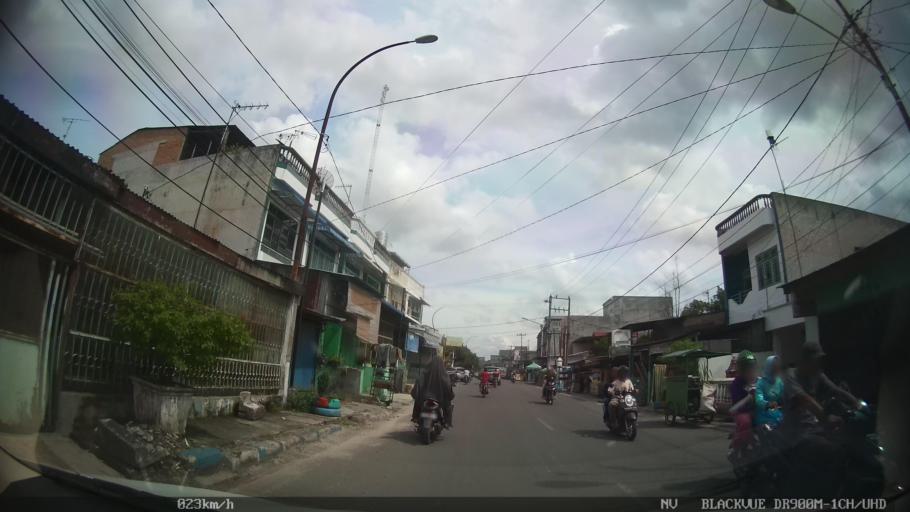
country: ID
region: North Sumatra
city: Percut
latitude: 3.5664
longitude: 98.8723
